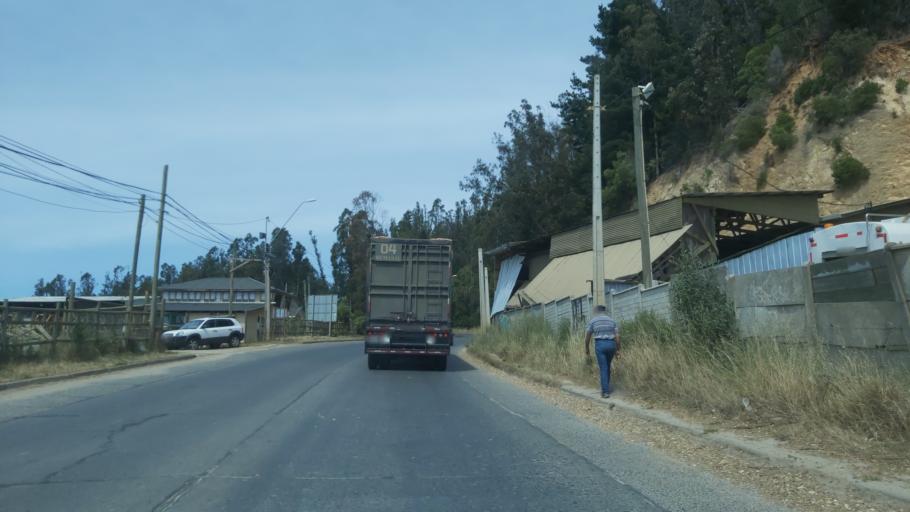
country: CL
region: Maule
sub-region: Provincia de Talca
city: Constitucion
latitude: -35.3461
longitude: -72.4176
